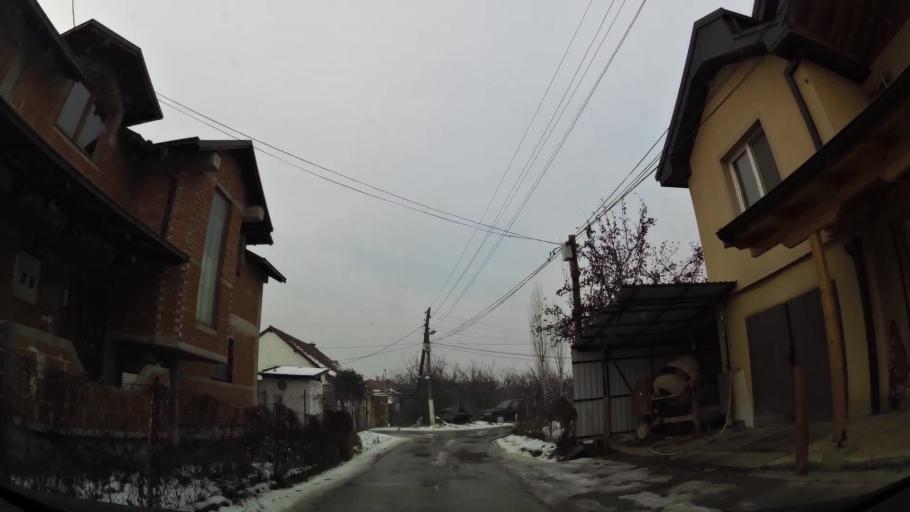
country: MK
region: Ilinden
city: Jurumleri
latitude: 41.9679
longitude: 21.5610
